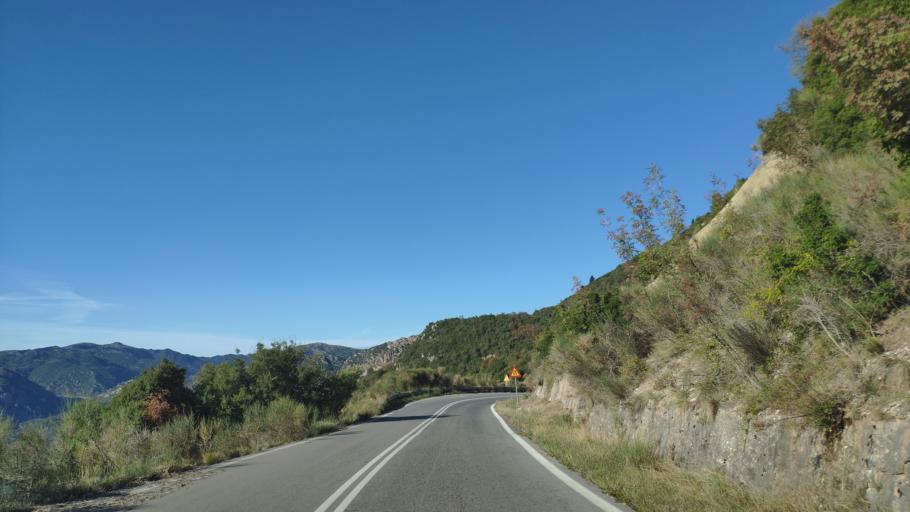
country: GR
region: Peloponnese
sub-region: Nomos Arkadias
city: Dimitsana
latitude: 37.5614
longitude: 22.0624
